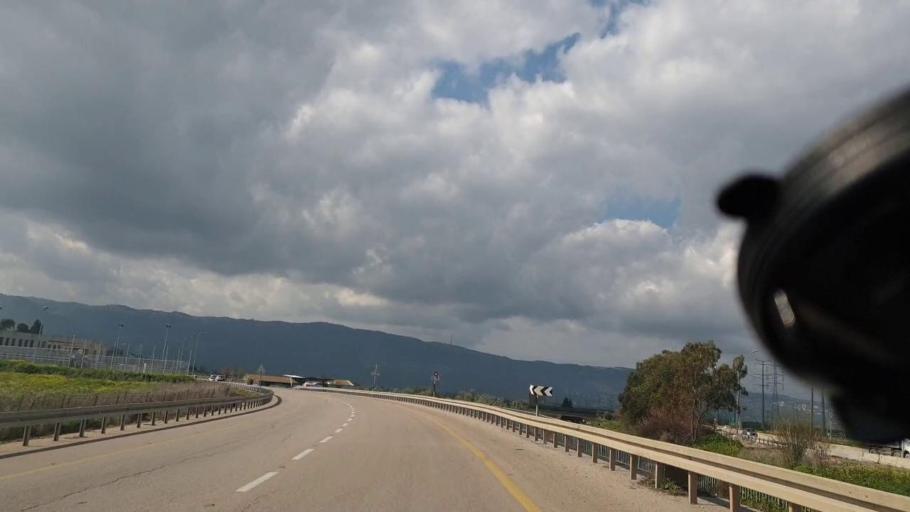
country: IL
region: Haifa
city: Ibtin
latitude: 32.7681
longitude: 35.1110
